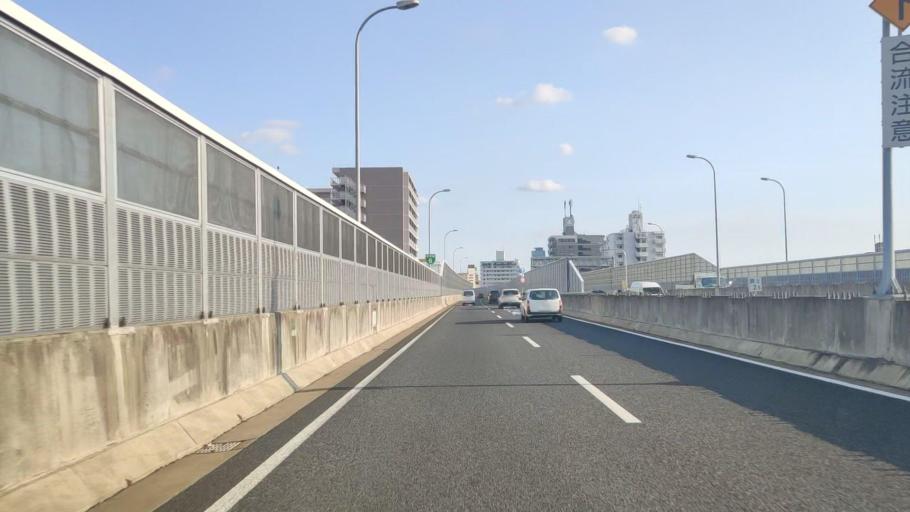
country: JP
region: Aichi
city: Nagoya-shi
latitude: 35.1996
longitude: 136.8909
